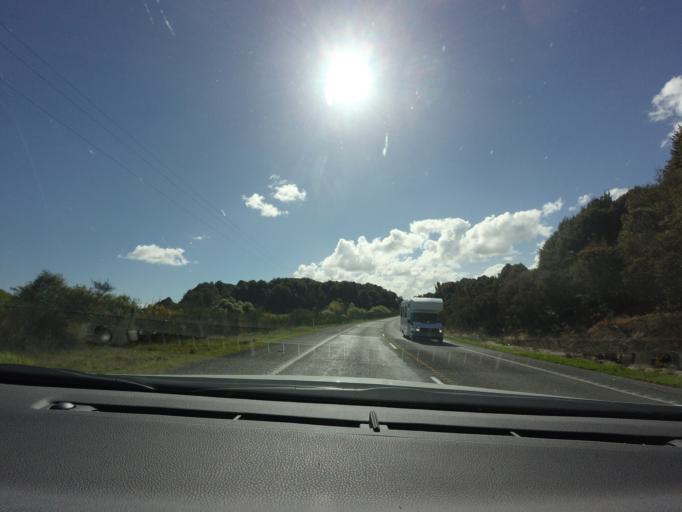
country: NZ
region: Bay of Plenty
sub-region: Rotorua District
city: Rotorua
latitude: -38.0366
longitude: 176.0314
